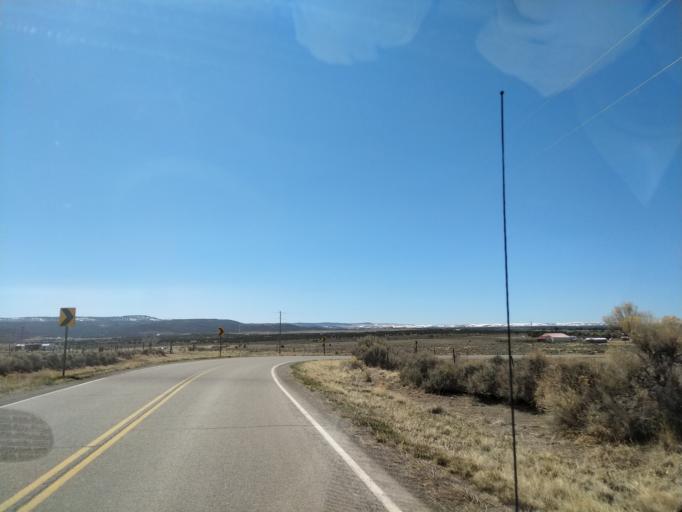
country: US
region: Colorado
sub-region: Mesa County
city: Redlands
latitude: 38.9912
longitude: -108.7506
